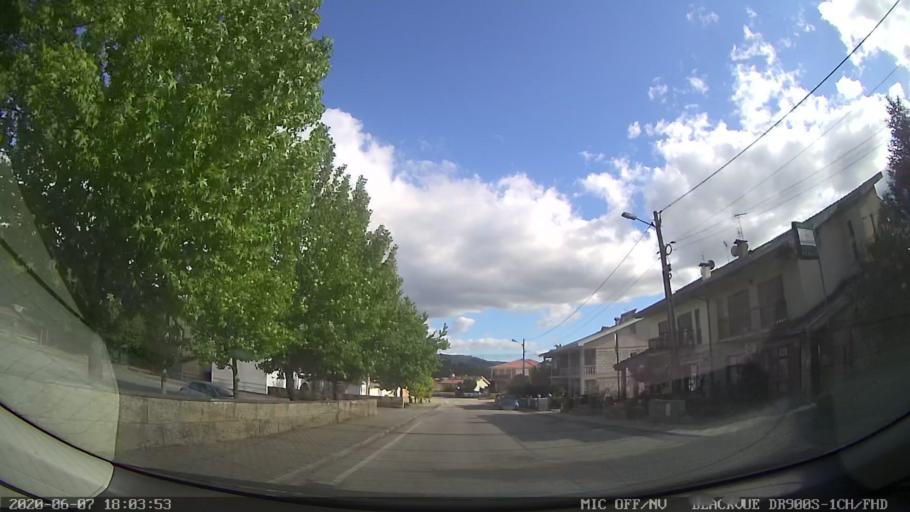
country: PT
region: Vila Real
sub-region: Vila Pouca de Aguiar
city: Vila Pouca de Aguiar
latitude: 41.4971
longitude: -7.6467
